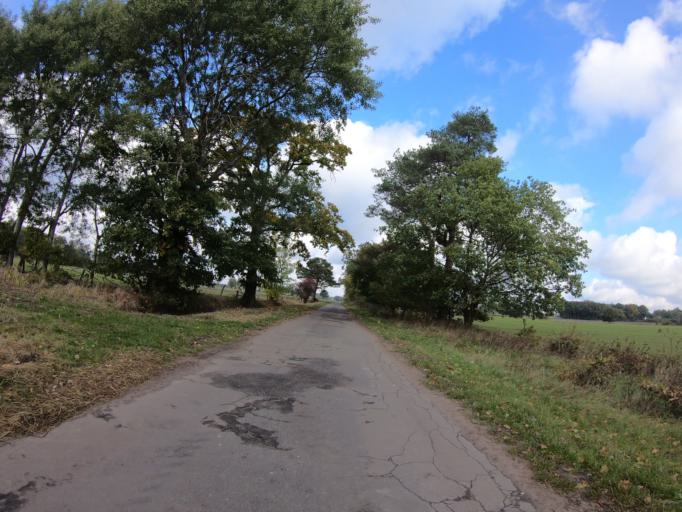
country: DE
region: Lower Saxony
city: Wagenhoff
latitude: 52.5276
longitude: 10.5375
